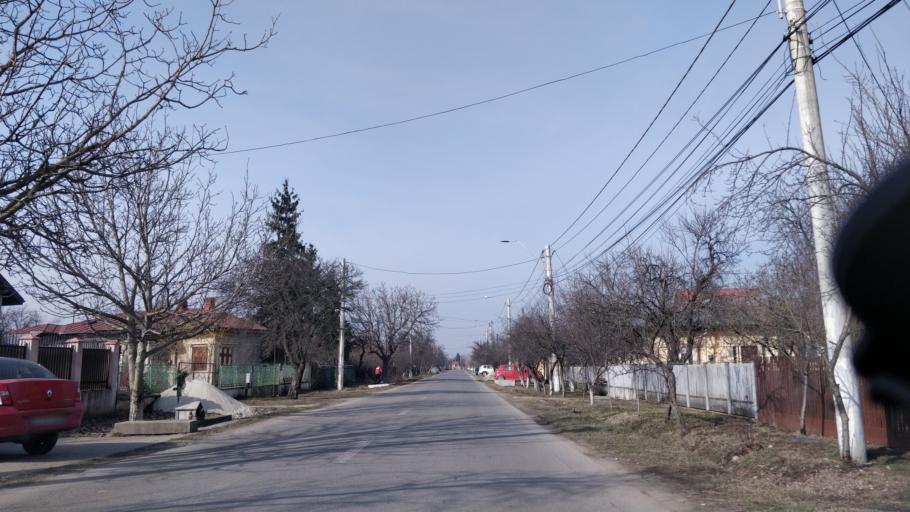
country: RO
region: Giurgiu
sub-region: Comuna Bolintin Vale
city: Bolintin Vale
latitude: 44.4612
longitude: 25.7794
